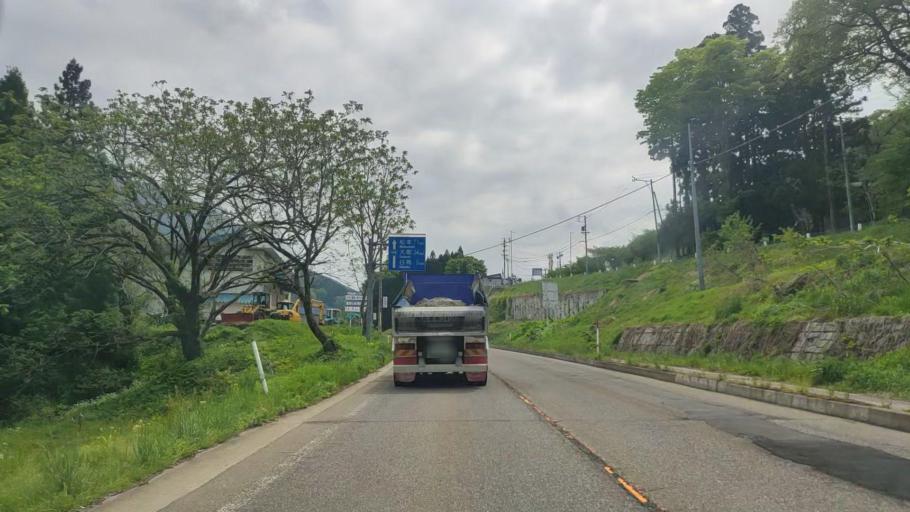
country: JP
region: Nagano
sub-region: Kitaazumi Gun
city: Hakuba
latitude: 36.7605
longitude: 137.8980
